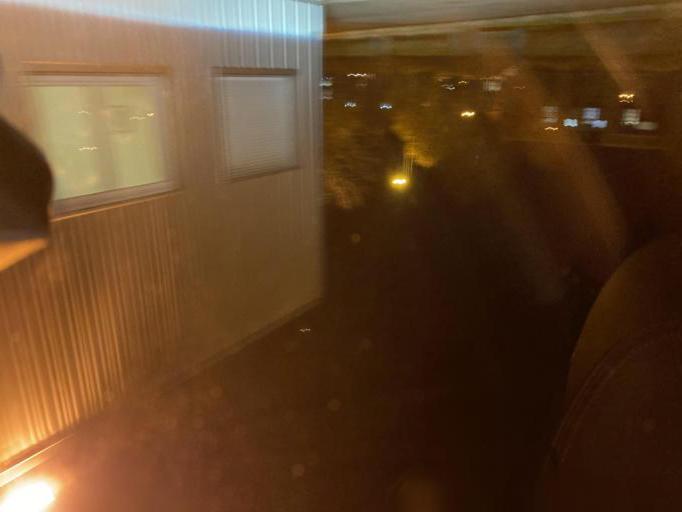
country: FR
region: Haute-Normandie
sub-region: Departement de l'Eure
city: Evreux
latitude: 49.0136
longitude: 1.1837
